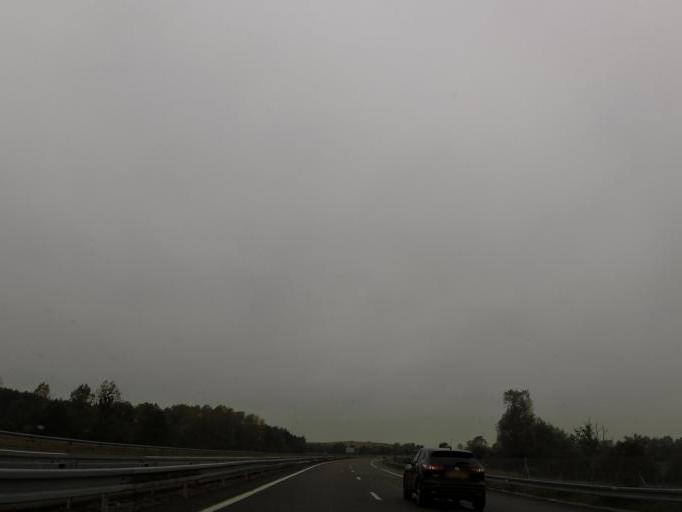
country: FR
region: Champagne-Ardenne
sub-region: Departement de la Marne
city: Sainte-Menehould
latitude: 49.0752
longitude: 4.8415
